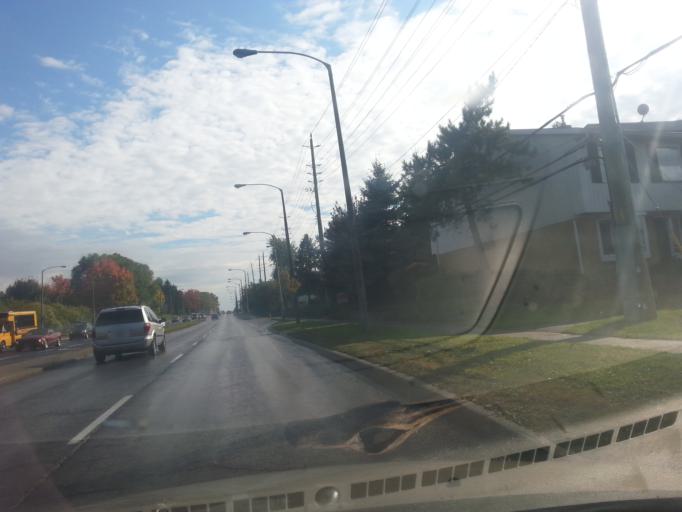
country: CA
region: Ontario
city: Bells Corners
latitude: 45.3406
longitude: -75.7879
